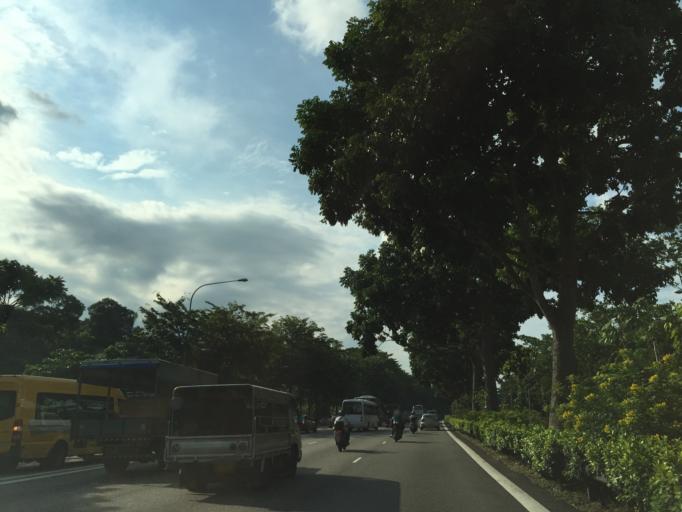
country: MY
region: Johor
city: Johor Bahru
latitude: 1.3930
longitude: 103.7741
